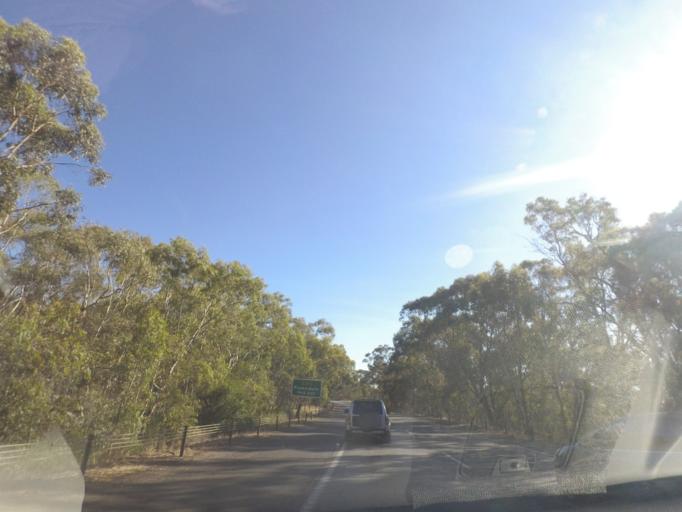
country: AU
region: Victoria
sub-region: Murrindindi
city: Kinglake West
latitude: -37.1772
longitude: 145.0713
